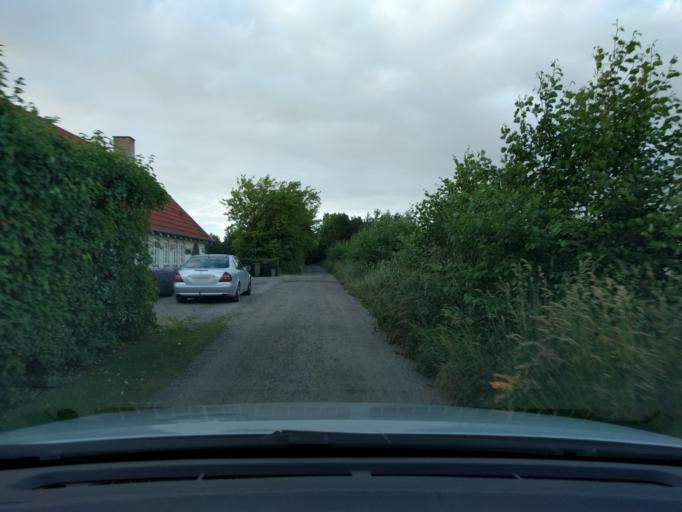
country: DK
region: South Denmark
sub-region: Odense Kommune
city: Bullerup
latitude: 55.4188
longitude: 10.4964
